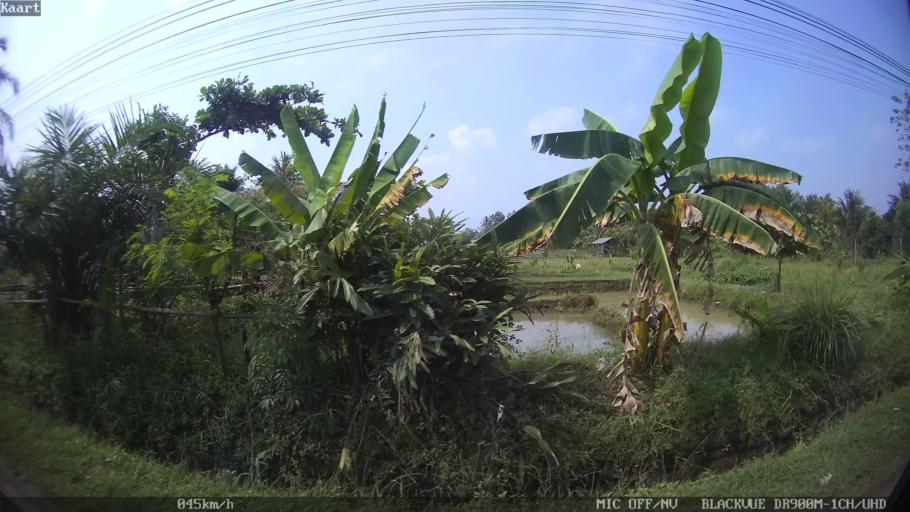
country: ID
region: Lampung
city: Gedongtataan
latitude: -5.3758
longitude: 105.0903
